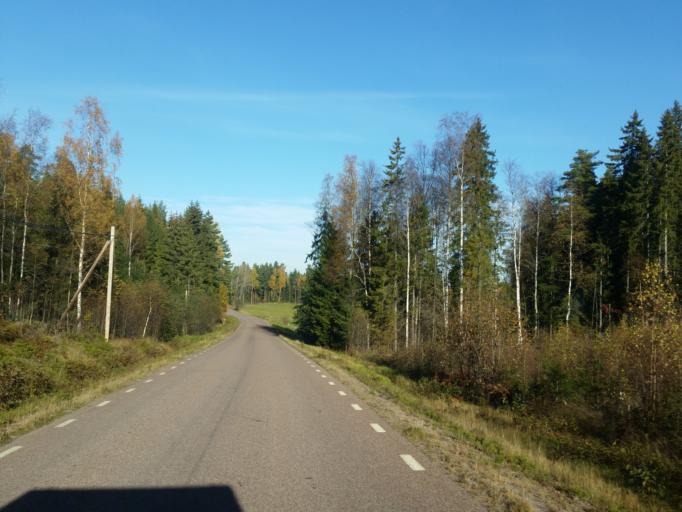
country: SE
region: Dalarna
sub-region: Borlange Kommun
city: Ornas
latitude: 60.4554
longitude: 15.6171
